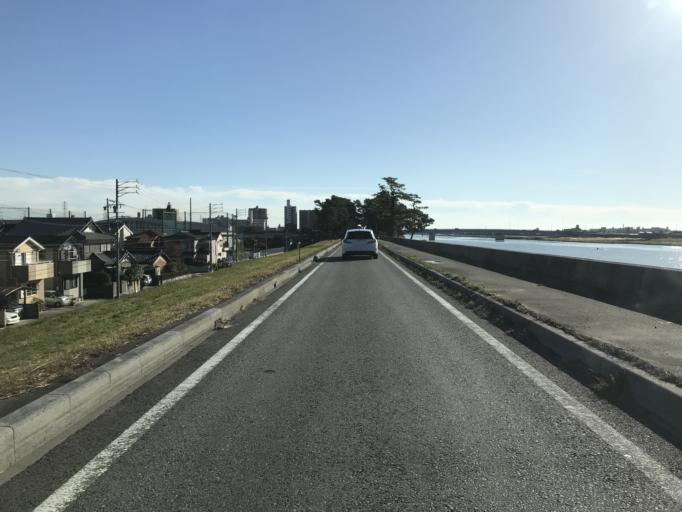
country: JP
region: Aichi
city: Kanie
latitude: 35.1294
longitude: 136.8388
